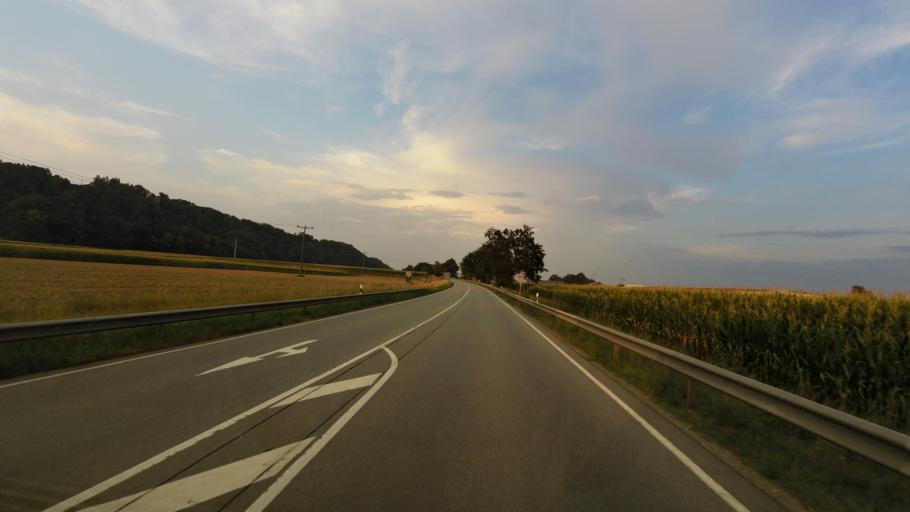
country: DE
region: Bavaria
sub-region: Lower Bavaria
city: Ering
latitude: 48.3046
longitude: 13.1489
